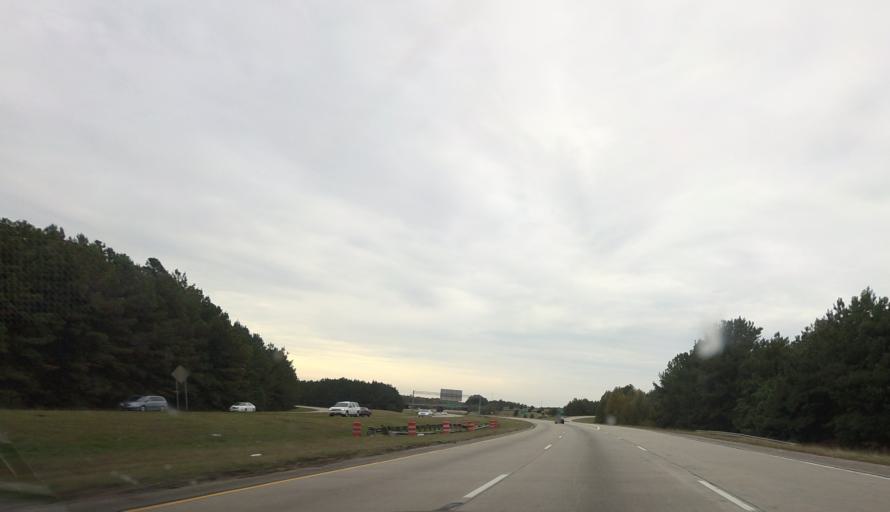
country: US
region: Alabama
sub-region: Russell County
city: Phenix City
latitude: 32.5372
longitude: -84.9740
